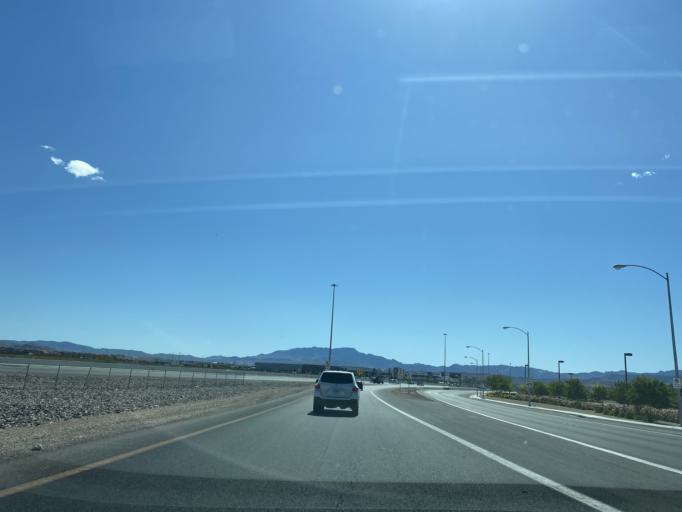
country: US
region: Nevada
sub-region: Clark County
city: Spring Valley
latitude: 36.0677
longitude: -115.2266
